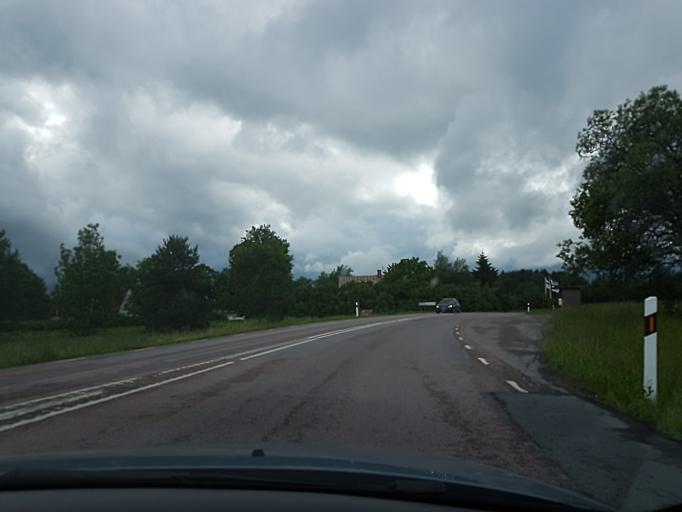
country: SE
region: Uppsala
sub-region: Osthammars Kommun
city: OEsthammar
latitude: 60.2433
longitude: 18.3484
